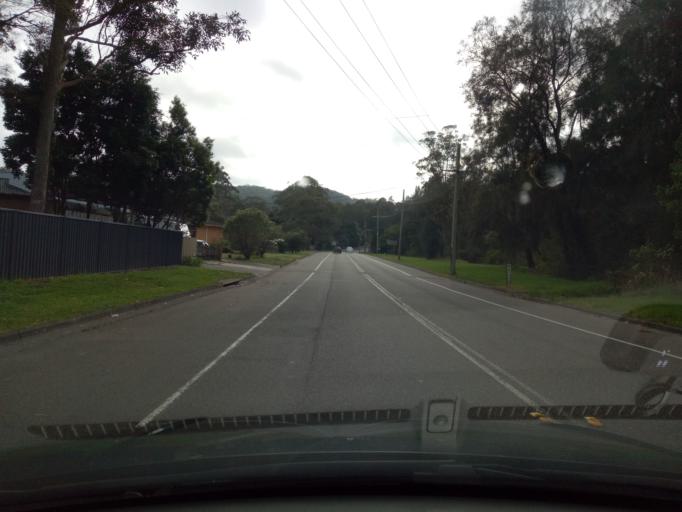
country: AU
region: New South Wales
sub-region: Gosford Shire
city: East Gosford
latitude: -33.4320
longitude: 151.3689
